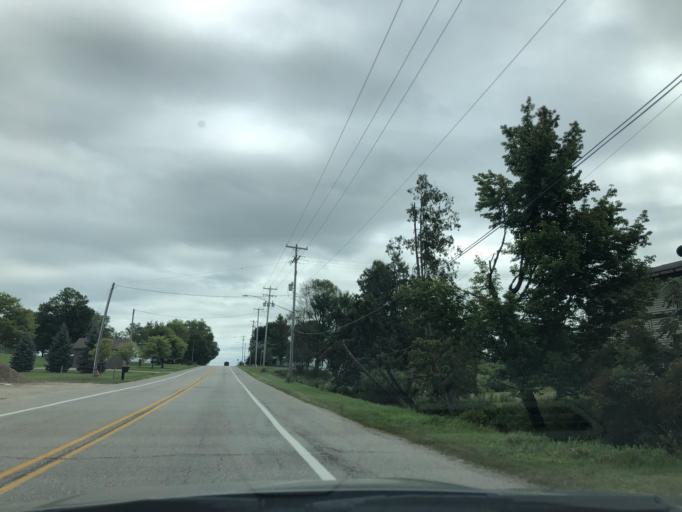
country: US
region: Michigan
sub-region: Missaukee County
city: Lake City
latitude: 44.1937
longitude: -85.2073
